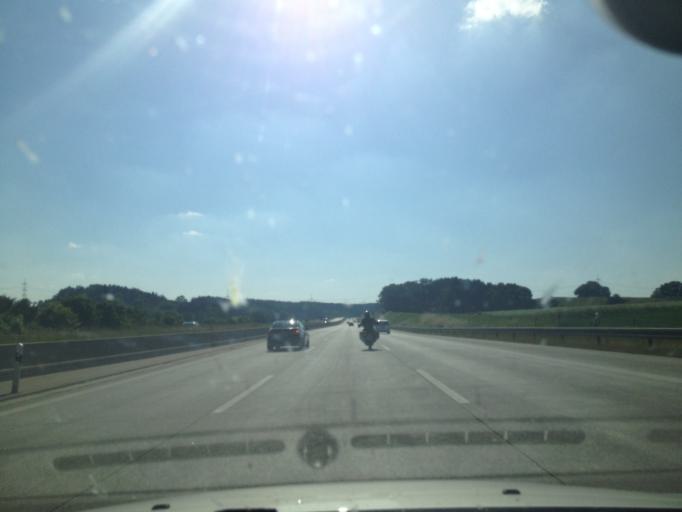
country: DE
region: Bavaria
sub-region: Swabia
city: Dasing
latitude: 48.3967
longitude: 11.0495
